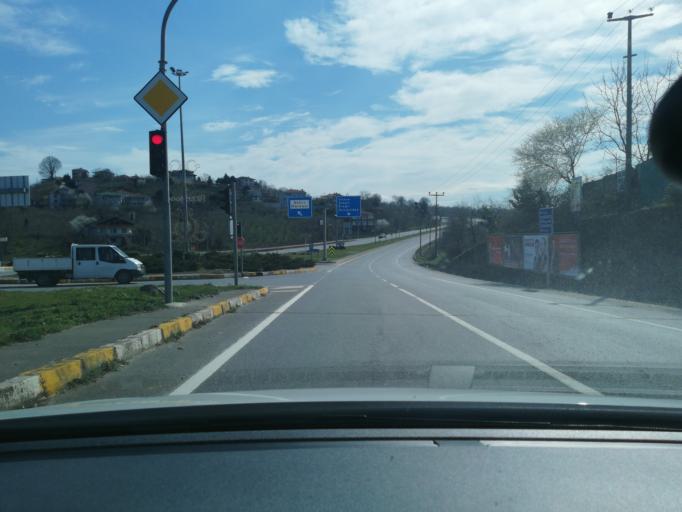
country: TR
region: Duzce
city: Akcakoca
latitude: 41.0860
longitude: 31.1532
